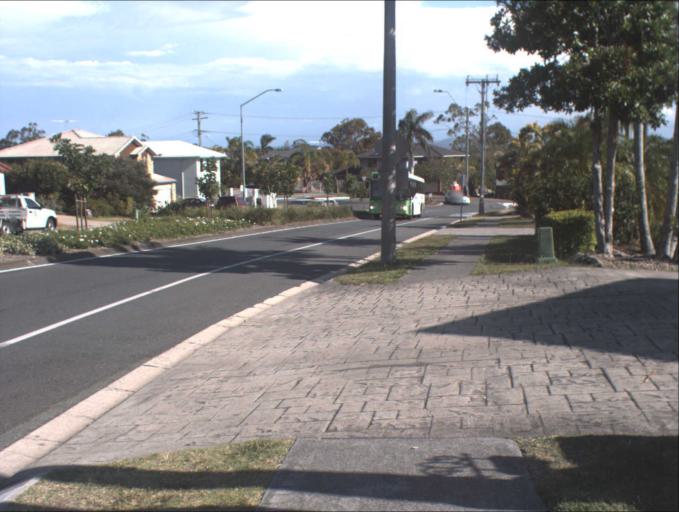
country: AU
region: Queensland
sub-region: Logan
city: Slacks Creek
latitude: -27.6500
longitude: 153.1834
